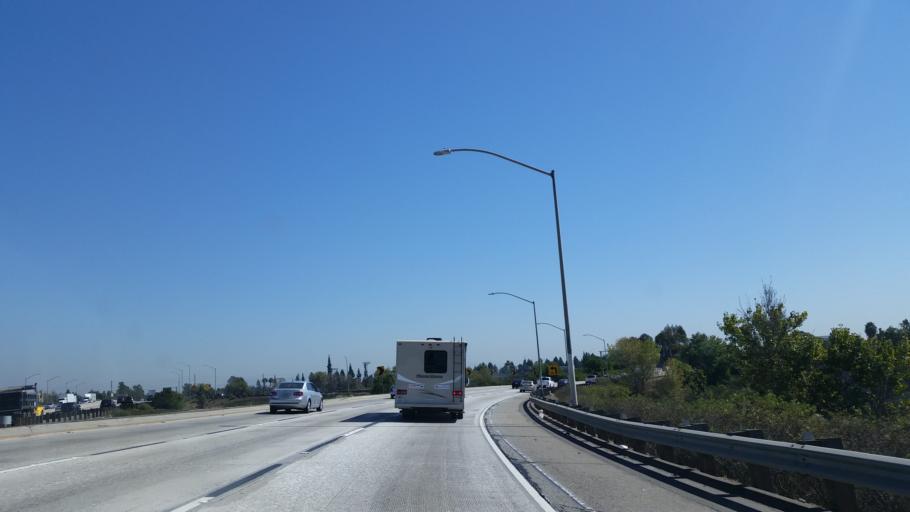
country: US
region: California
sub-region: Los Angeles County
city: Bellflower
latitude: 33.8762
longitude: -118.1064
